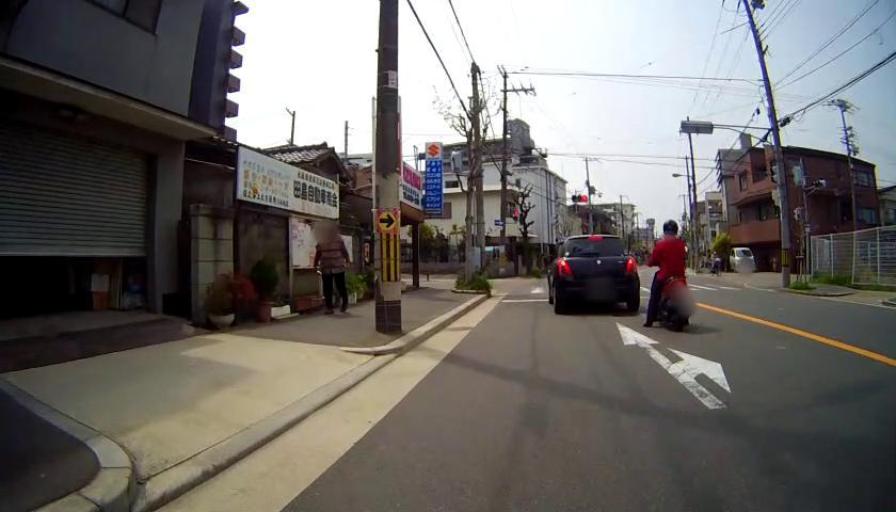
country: JP
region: Osaka
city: Suita
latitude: 34.7503
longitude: 135.5401
